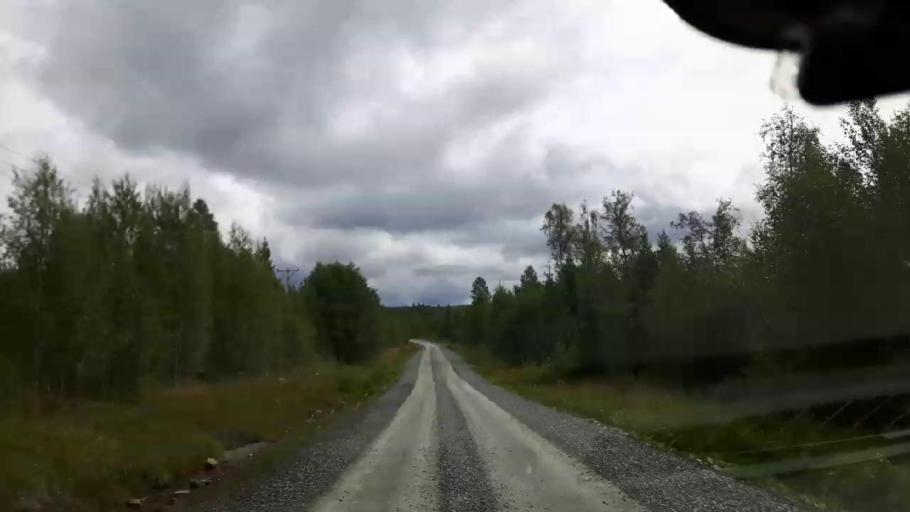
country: SE
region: Jaemtland
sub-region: Krokoms Kommun
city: Valla
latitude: 63.6057
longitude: 14.1252
